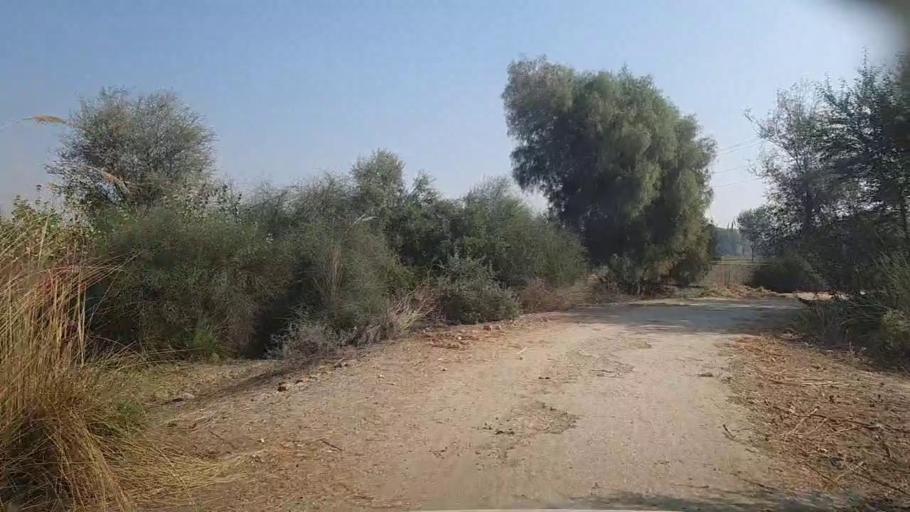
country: PK
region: Sindh
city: Kandiari
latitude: 26.9409
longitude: 68.5431
